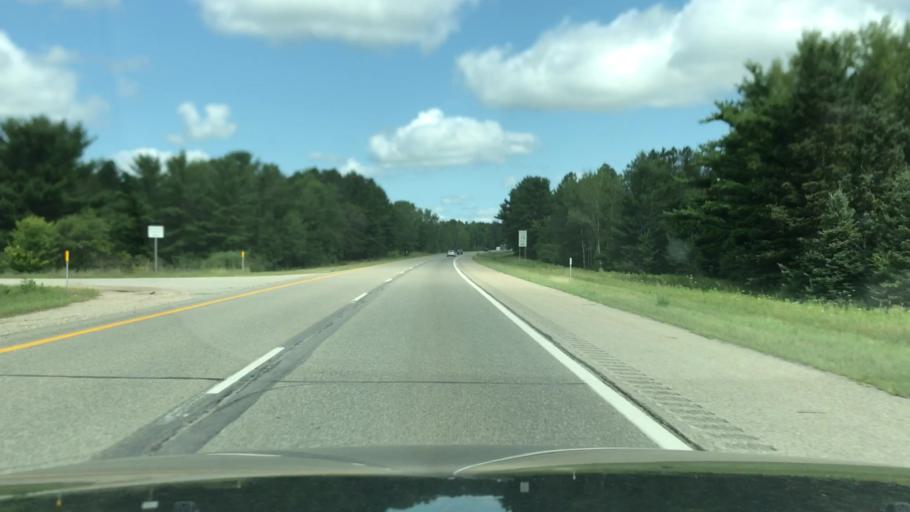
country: US
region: Michigan
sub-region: Mecosta County
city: Big Rapids
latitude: 43.6962
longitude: -85.5253
